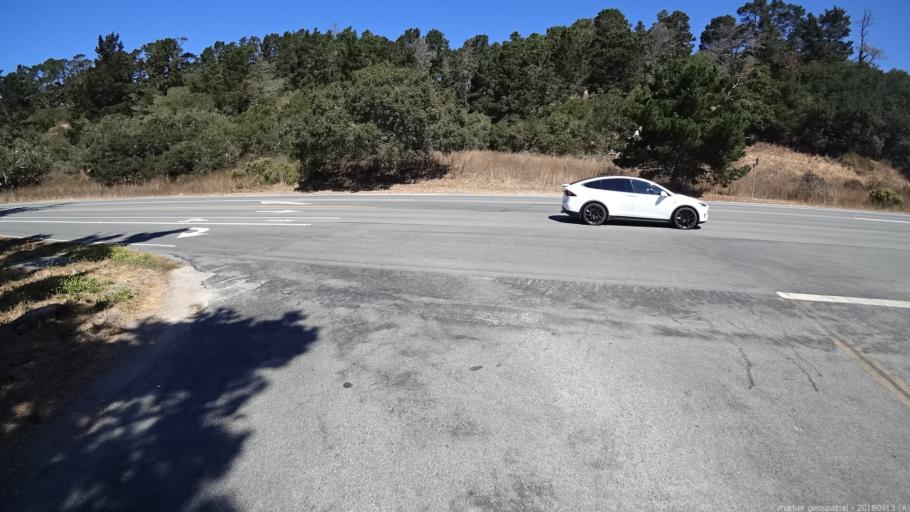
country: US
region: California
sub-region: Monterey County
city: Carmel-by-the-Sea
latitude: 36.5400
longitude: -121.8653
